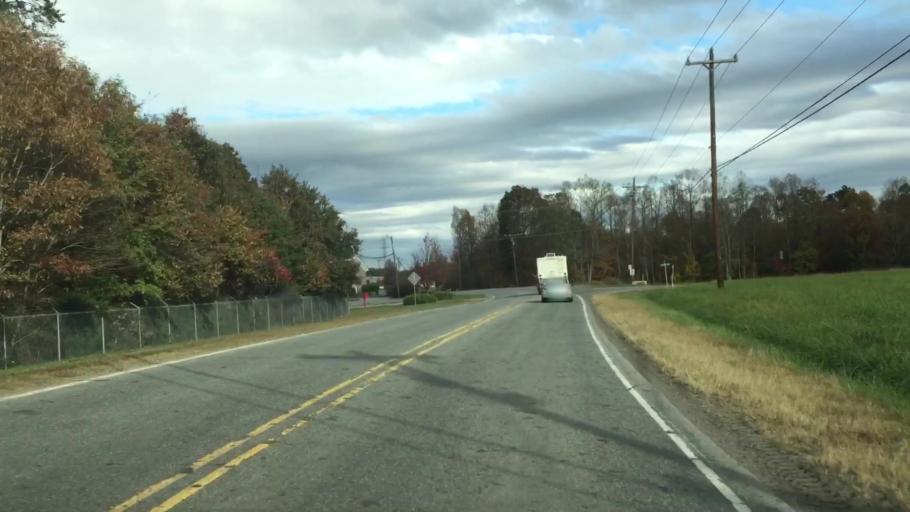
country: US
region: North Carolina
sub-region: Guilford County
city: Summerfield
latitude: 36.2407
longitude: -79.9312
